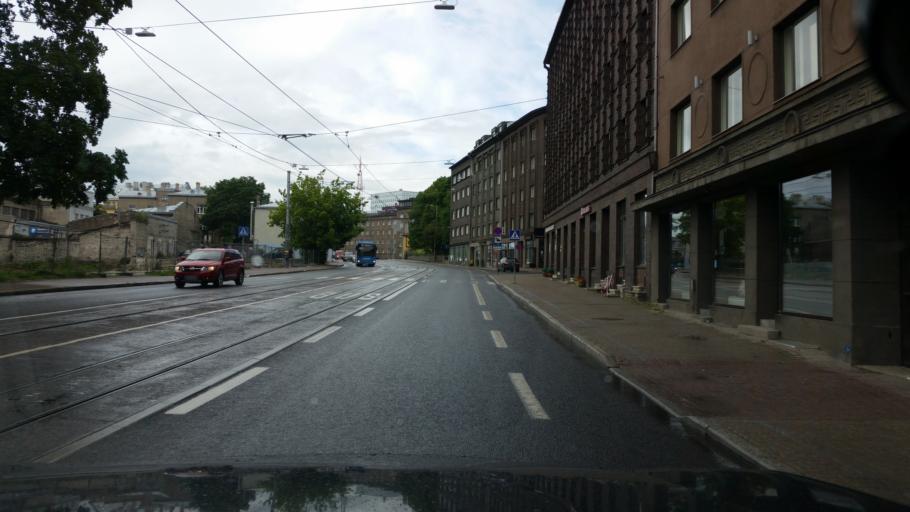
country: EE
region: Harju
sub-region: Tallinna linn
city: Tallinn
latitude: 59.4304
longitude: 24.7450
